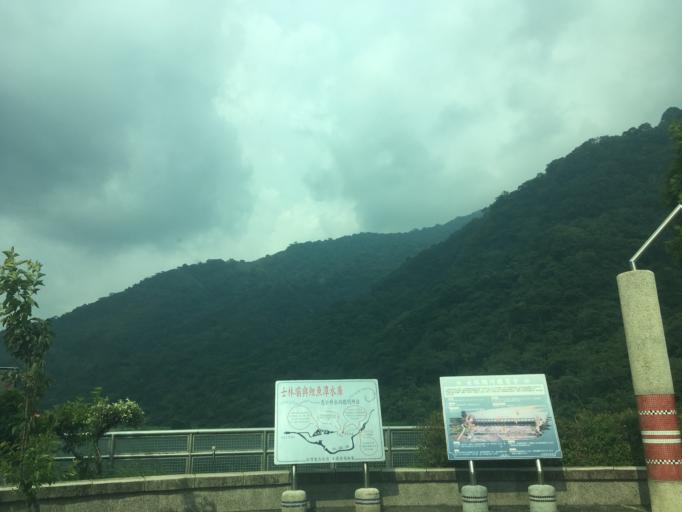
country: TW
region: Taiwan
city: Fengyuan
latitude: 24.3432
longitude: 120.9373
